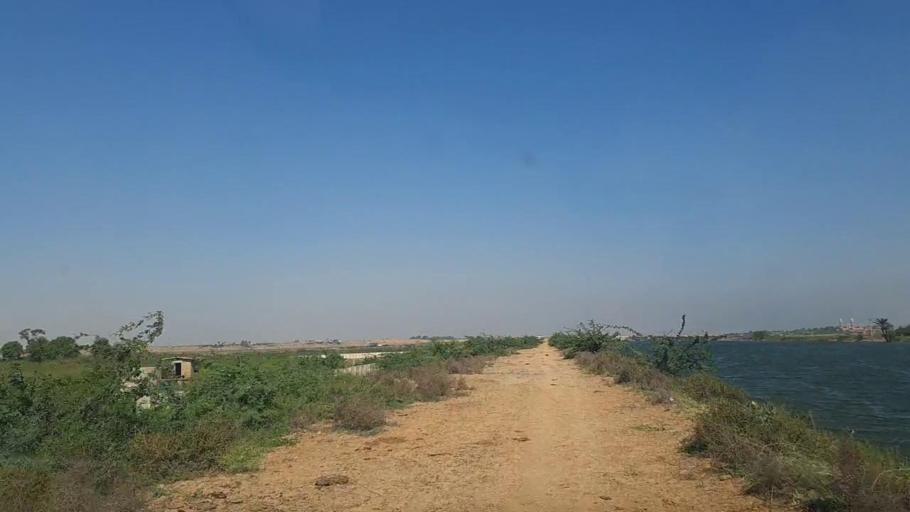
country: PK
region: Sindh
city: Thatta
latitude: 24.8201
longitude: 67.9898
